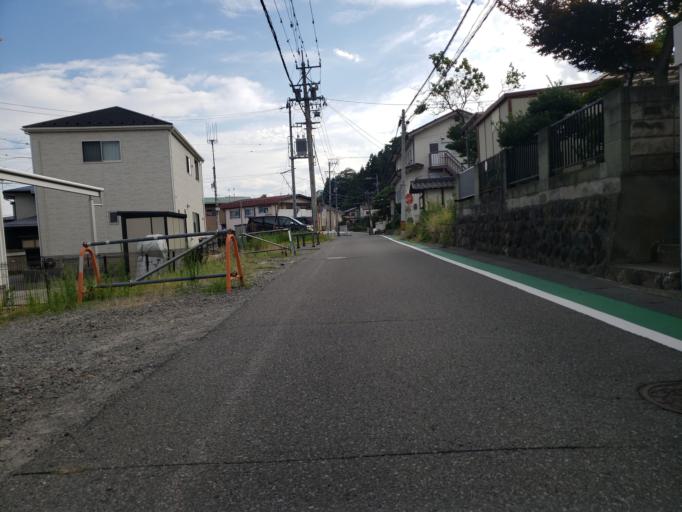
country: JP
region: Nagano
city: Nagano-shi
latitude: 36.6451
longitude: 138.1769
